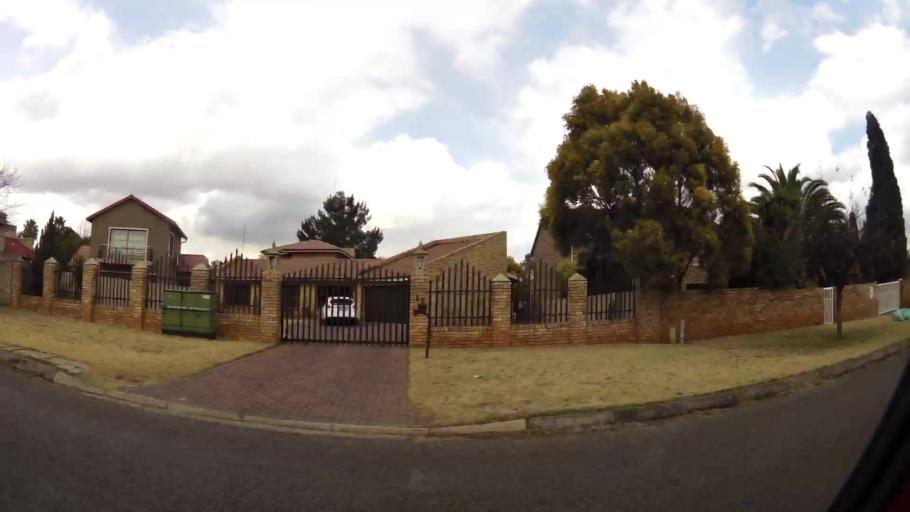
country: ZA
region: Gauteng
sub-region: Sedibeng District Municipality
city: Vanderbijlpark
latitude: -26.7335
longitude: 27.8444
